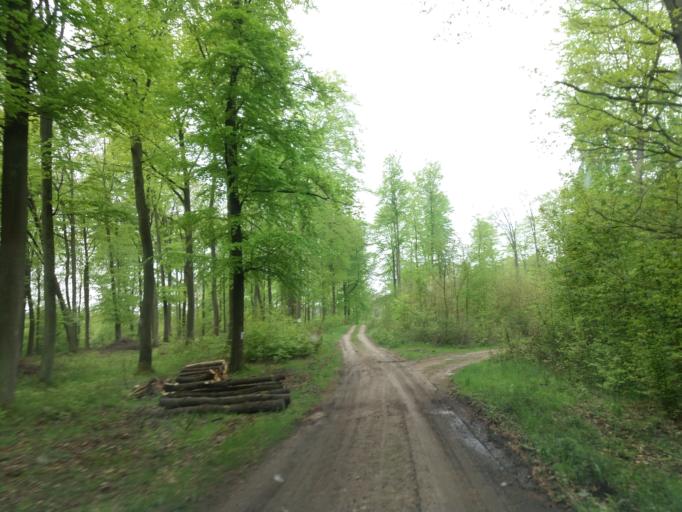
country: PL
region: West Pomeranian Voivodeship
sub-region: Powiat choszczenski
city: Bierzwnik
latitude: 53.0380
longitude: 15.5842
